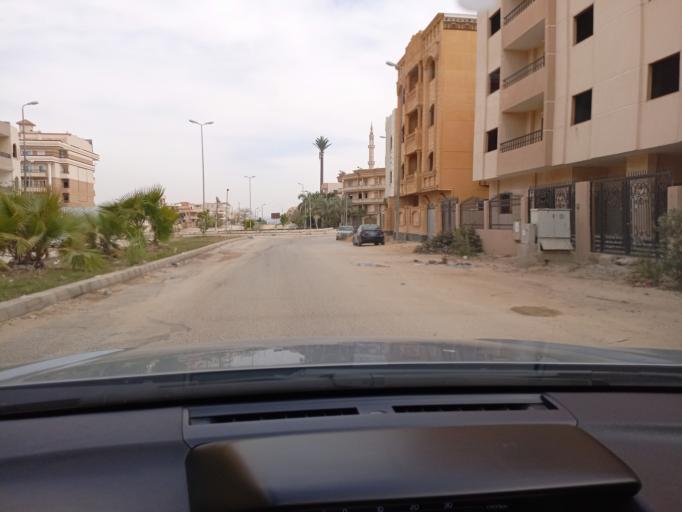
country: EG
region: Muhafazat al Qalyubiyah
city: Al Khankah
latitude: 30.2459
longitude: 31.4975
